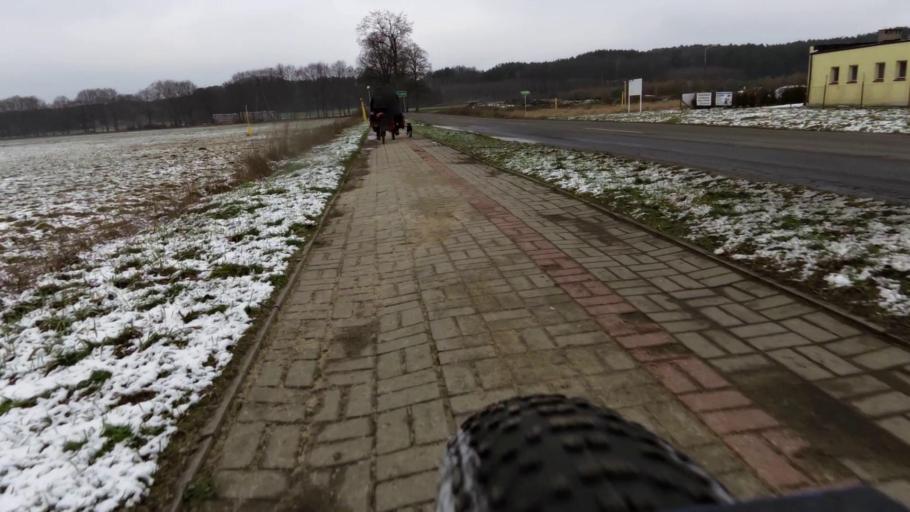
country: PL
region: West Pomeranian Voivodeship
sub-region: Powiat walecki
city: Miroslawiec
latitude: 53.3512
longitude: 16.0862
